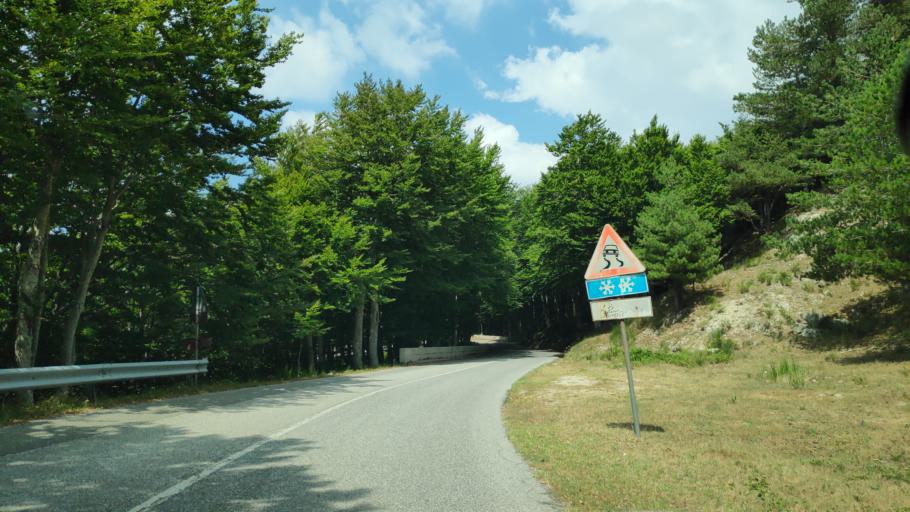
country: IT
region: Calabria
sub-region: Provincia di Vibo-Valentia
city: Mongiana
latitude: 38.5136
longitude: 16.3455
